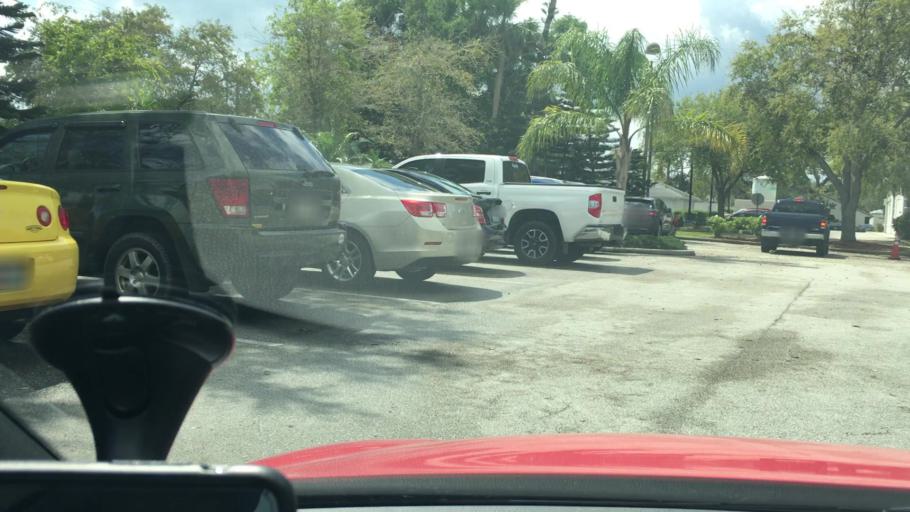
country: US
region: Florida
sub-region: Volusia County
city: New Smyrna Beach
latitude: 29.0195
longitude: -80.9217
